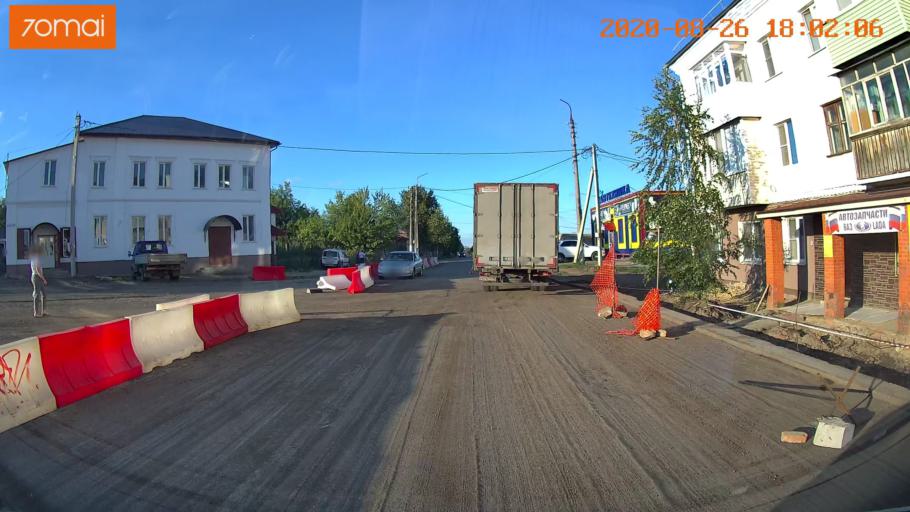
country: RU
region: Tula
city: Yefremov
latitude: 53.1380
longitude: 38.1197
